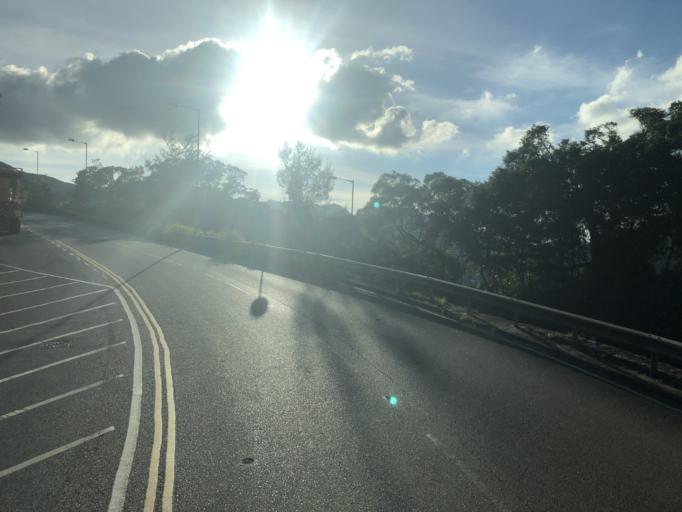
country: HK
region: Sai Kung
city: Sai Kung
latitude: 22.3433
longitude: 114.2507
